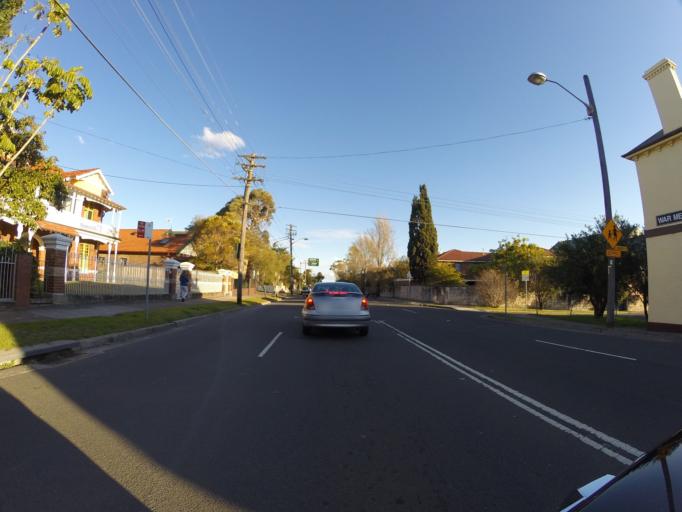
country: AU
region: New South Wales
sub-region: Waverley
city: Bondi Junction
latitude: -33.8980
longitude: 151.2541
